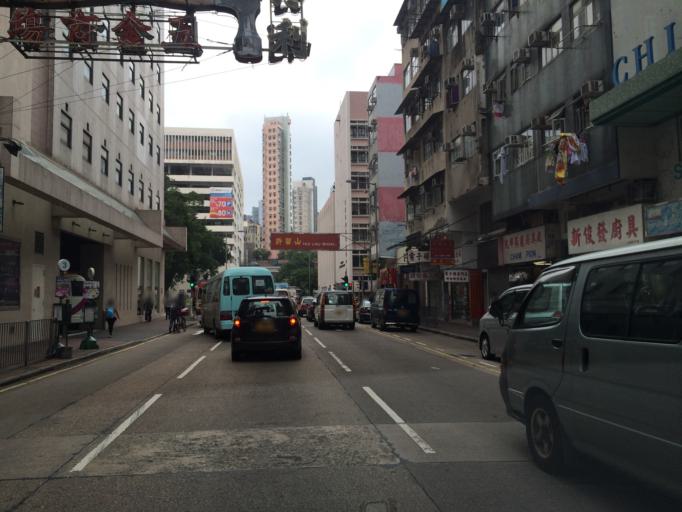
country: HK
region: Kowloon City
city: Kowloon
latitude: 22.3107
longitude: 114.1700
